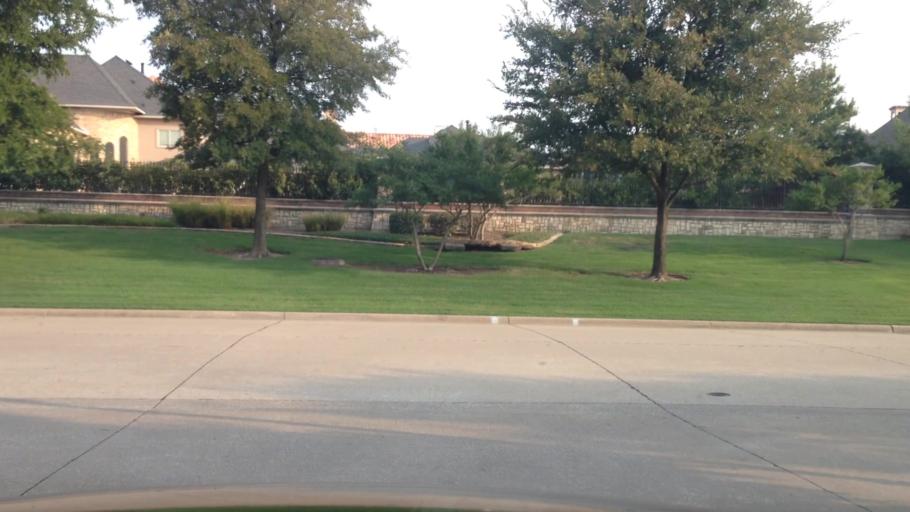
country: US
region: Texas
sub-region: Collin County
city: Frisco
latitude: 33.1261
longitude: -96.8388
